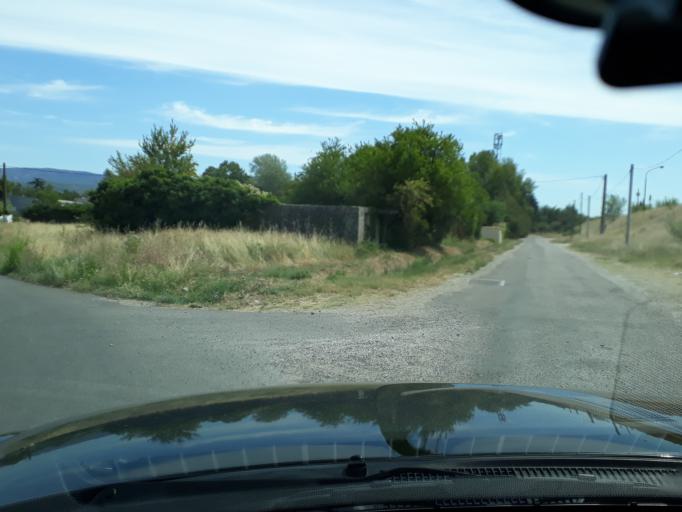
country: FR
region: Provence-Alpes-Cote d'Azur
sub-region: Departement du Vaucluse
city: Carpentras
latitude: 44.0386
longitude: 5.0463
